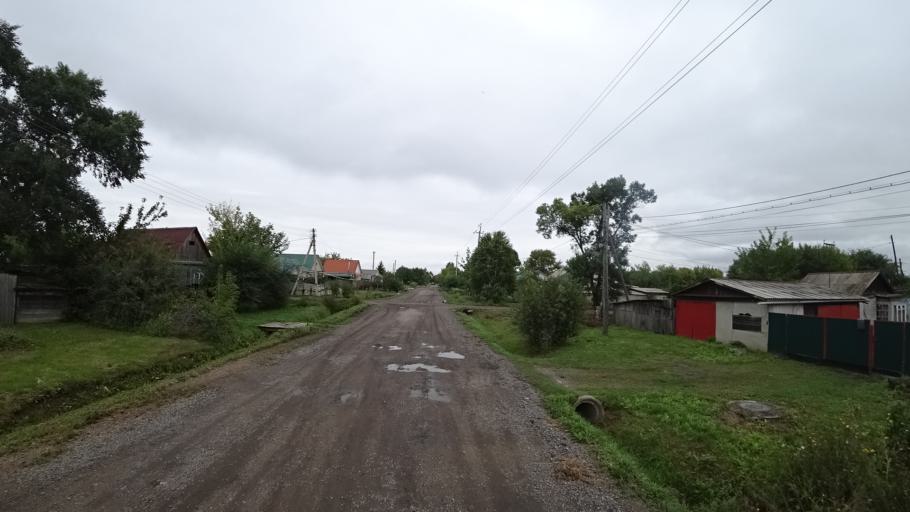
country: RU
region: Primorskiy
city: Chernigovka
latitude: 44.3445
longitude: 132.5825
